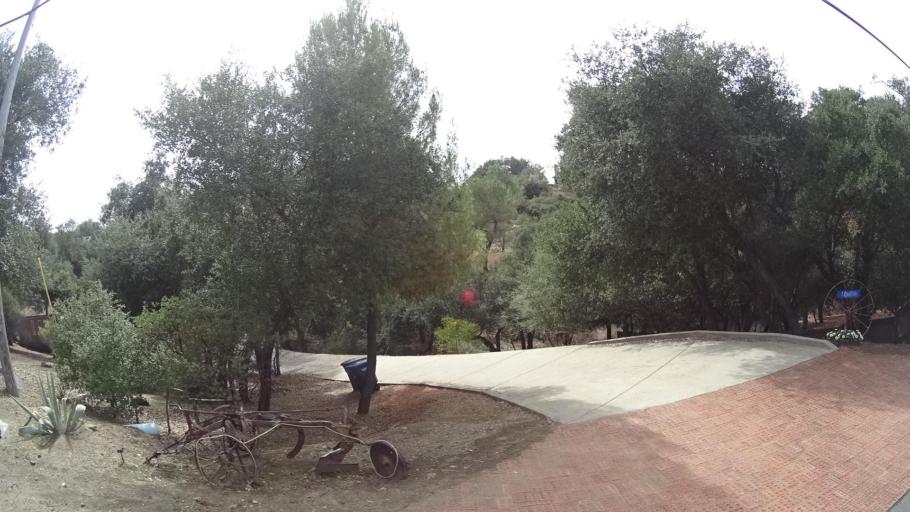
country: US
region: California
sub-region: San Diego County
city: Descanso
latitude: 32.8745
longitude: -116.6364
